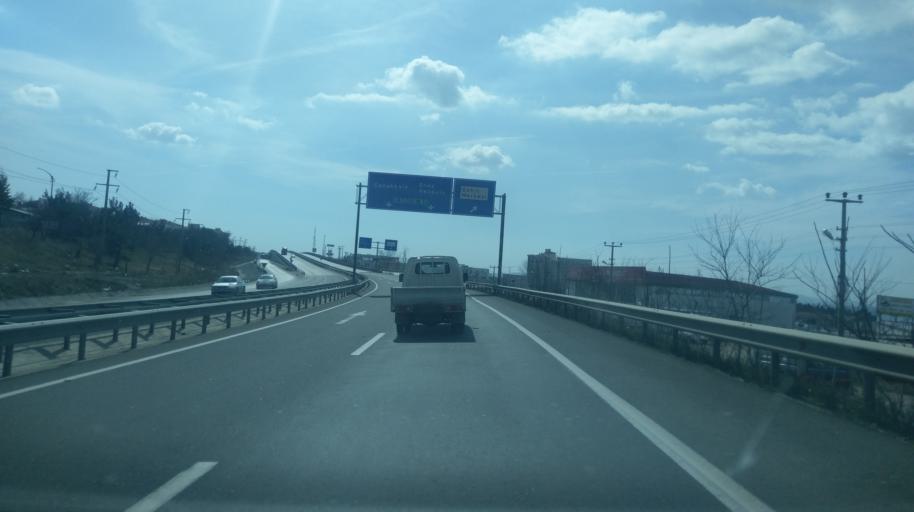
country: TR
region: Edirne
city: Kesan
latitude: 40.8631
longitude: 26.6220
